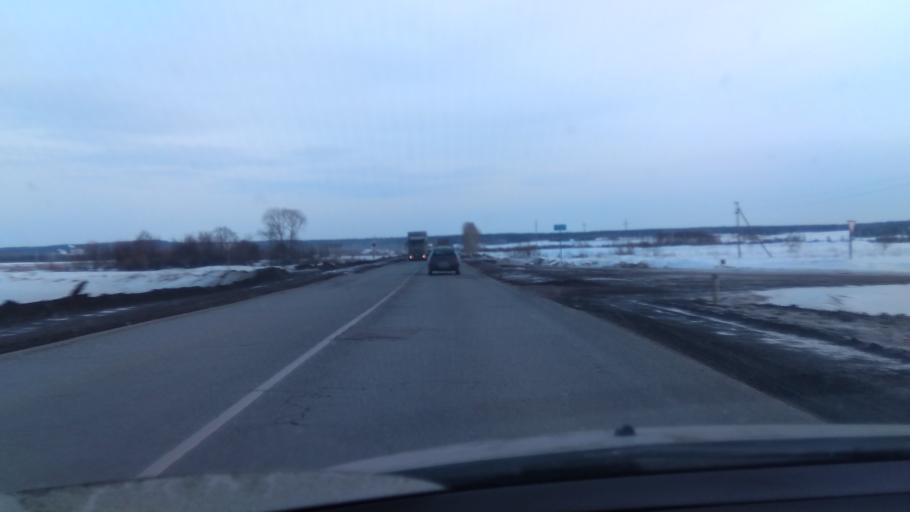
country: RU
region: Perm
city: Kukushtan
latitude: 57.5108
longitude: 56.6445
